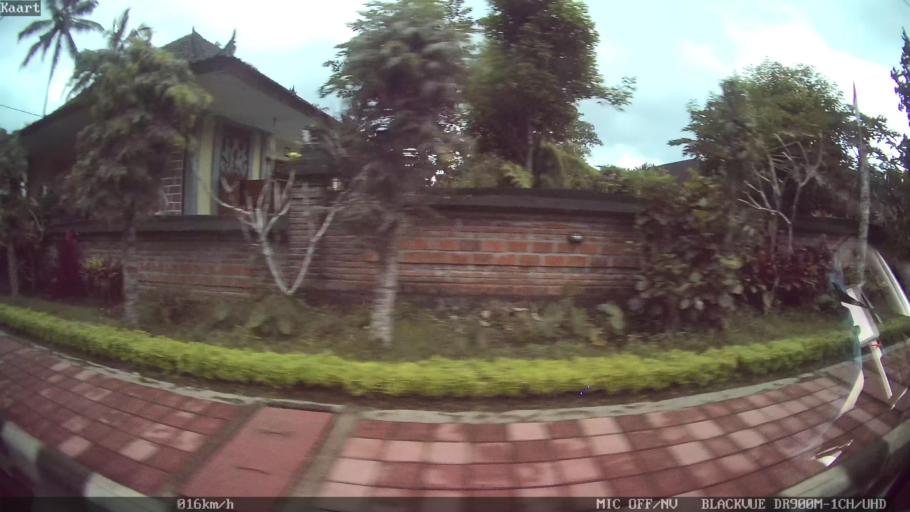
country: ID
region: Bali
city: Banjar Wangsian
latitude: -8.4330
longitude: 115.4255
